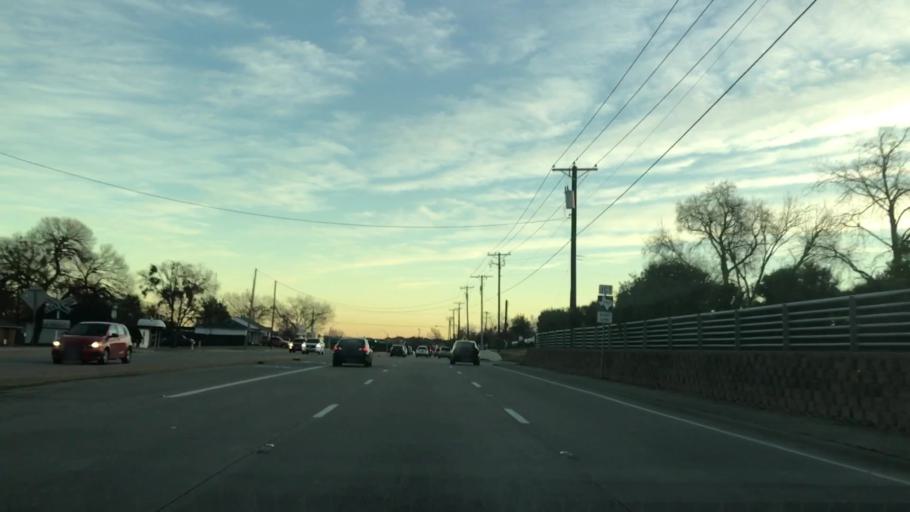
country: US
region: Texas
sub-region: Rockwall County
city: Rockwall
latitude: 32.9237
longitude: -96.4605
